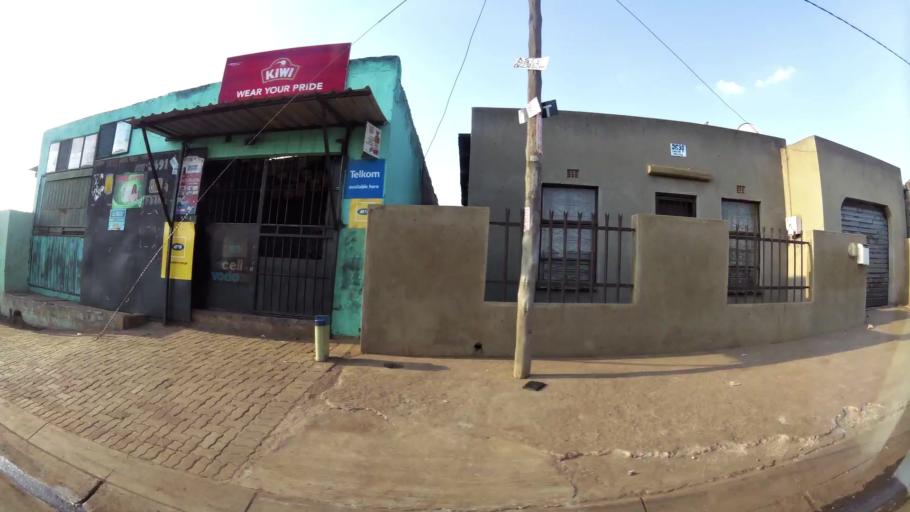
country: ZA
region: Gauteng
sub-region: Ekurhuleni Metropolitan Municipality
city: Tembisa
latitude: -25.9654
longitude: 28.2067
